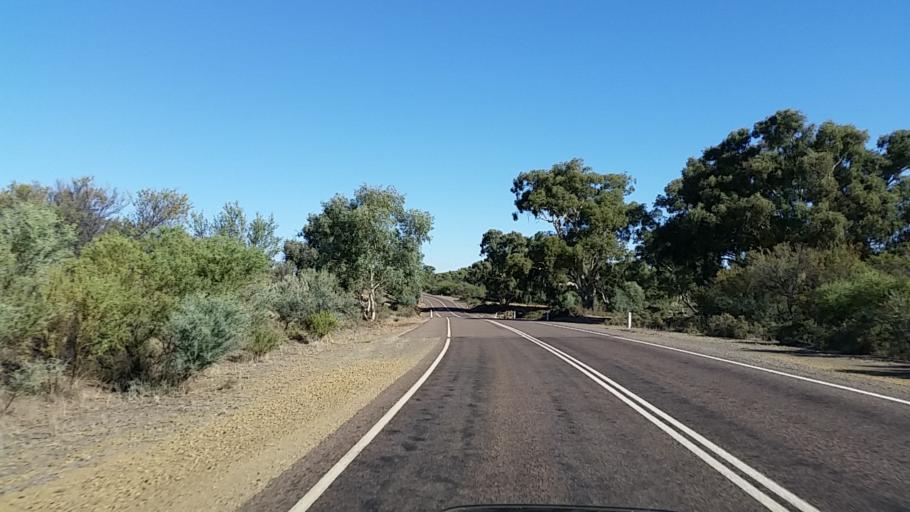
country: AU
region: South Australia
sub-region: Flinders Ranges
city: Quorn
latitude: -32.3307
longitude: 138.4741
